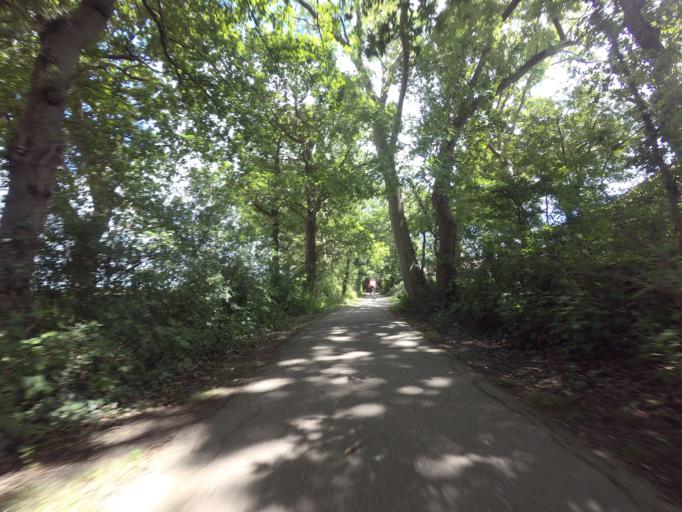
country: GB
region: England
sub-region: East Sussex
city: Hailsham
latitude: 50.8249
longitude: 0.2531
